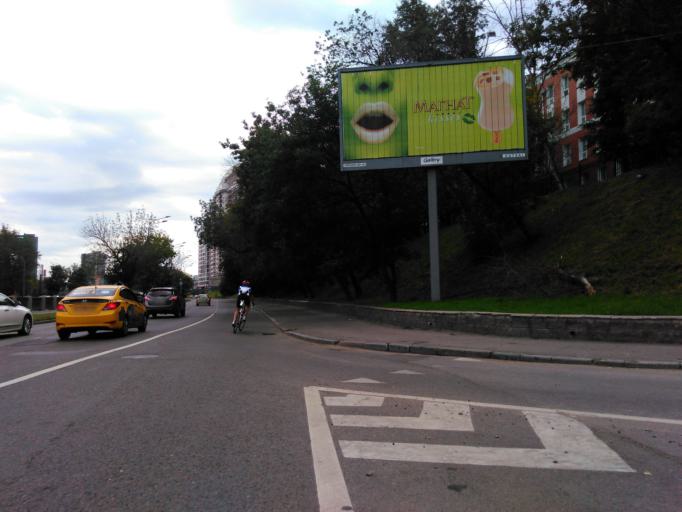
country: RU
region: Moscow
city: Lefortovo
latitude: 55.7885
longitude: 37.6987
